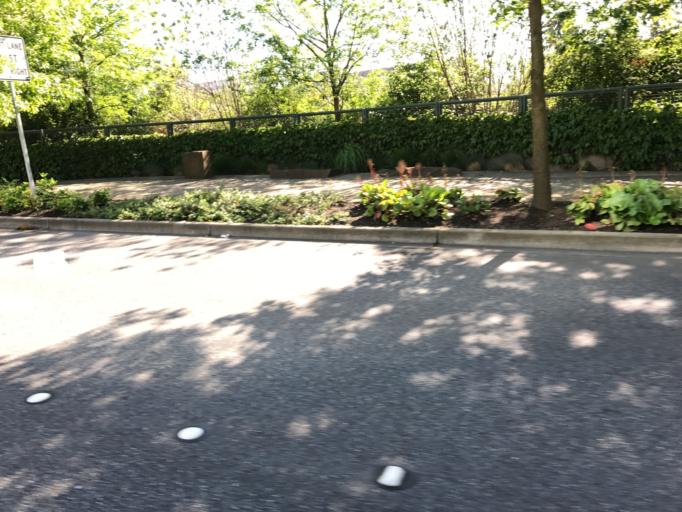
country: US
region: Washington
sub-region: King County
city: Bellevue
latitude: 47.6188
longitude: -122.1909
